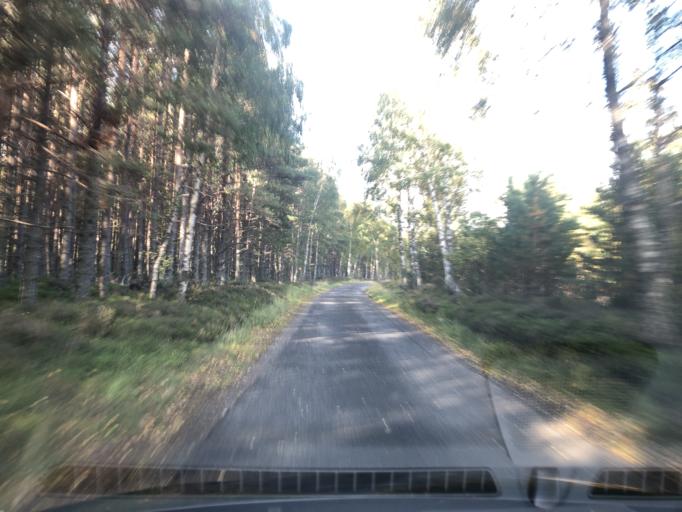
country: GB
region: Scotland
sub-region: Highland
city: Aviemore
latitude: 57.0700
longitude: -3.9021
